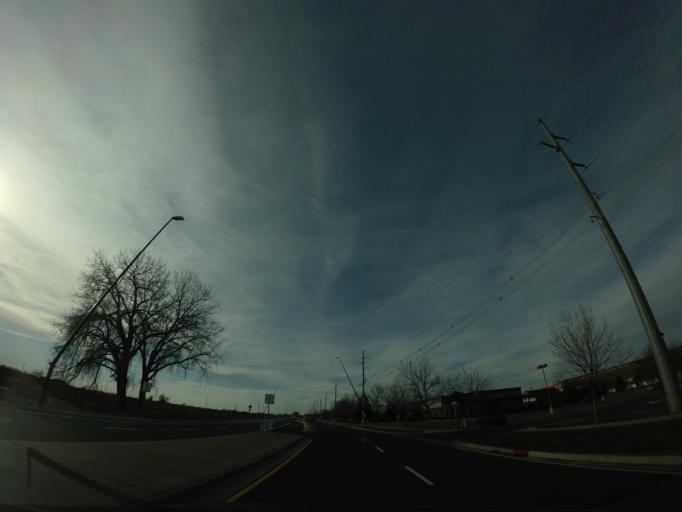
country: US
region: Montana
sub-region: Yellowstone County
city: Billings
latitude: 45.7843
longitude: -108.6129
